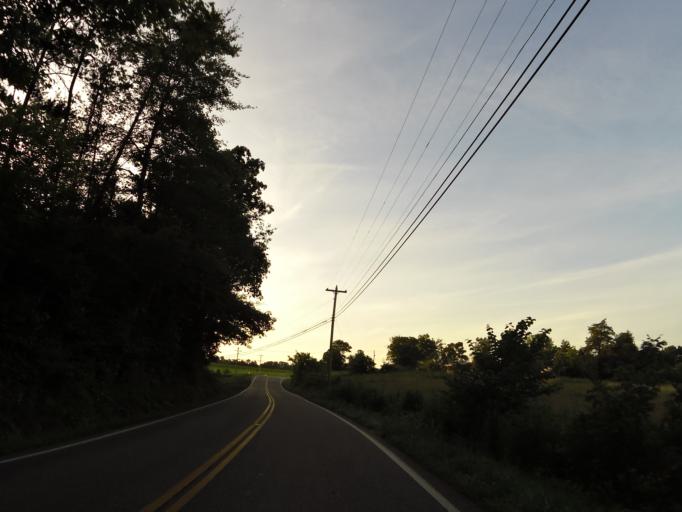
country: US
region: Tennessee
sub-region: Blount County
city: Maryville
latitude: 35.6765
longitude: -83.9740
